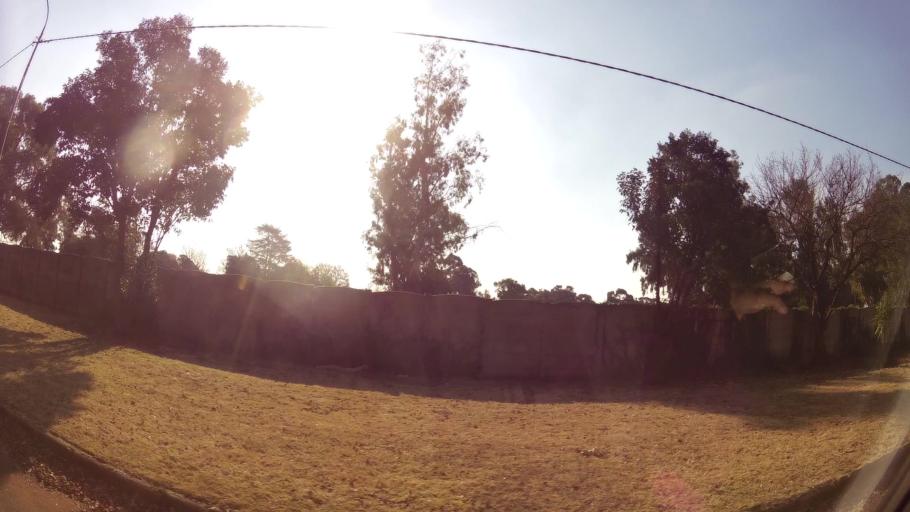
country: ZA
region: Gauteng
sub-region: Ekurhuleni Metropolitan Municipality
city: Brakpan
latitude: -26.2297
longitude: 28.3571
